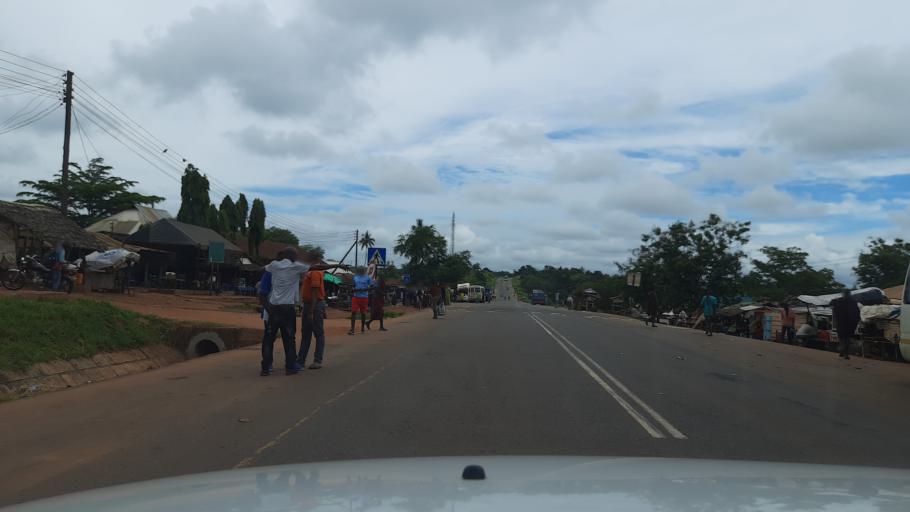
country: TZ
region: Pwani
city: Lugoba
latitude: -6.0810
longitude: 38.2435
